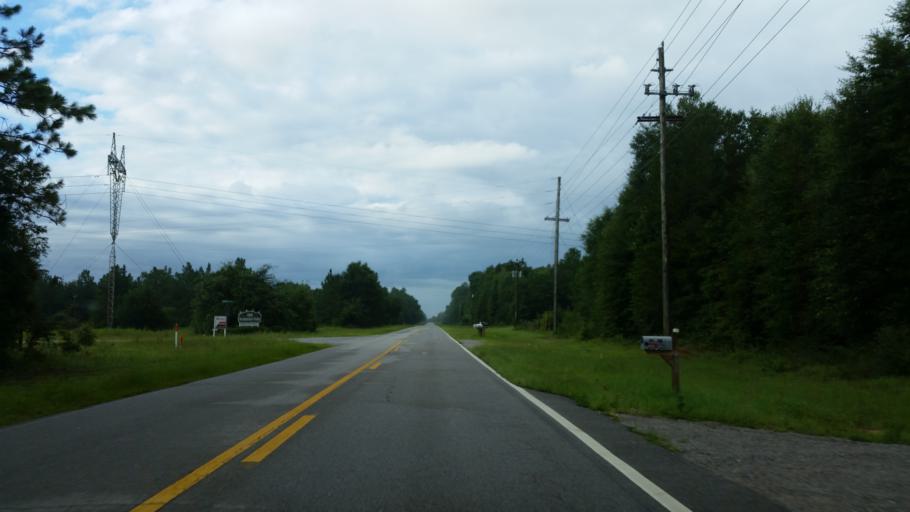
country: US
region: Florida
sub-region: Okaloosa County
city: Crestview
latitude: 30.6945
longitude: -86.7517
